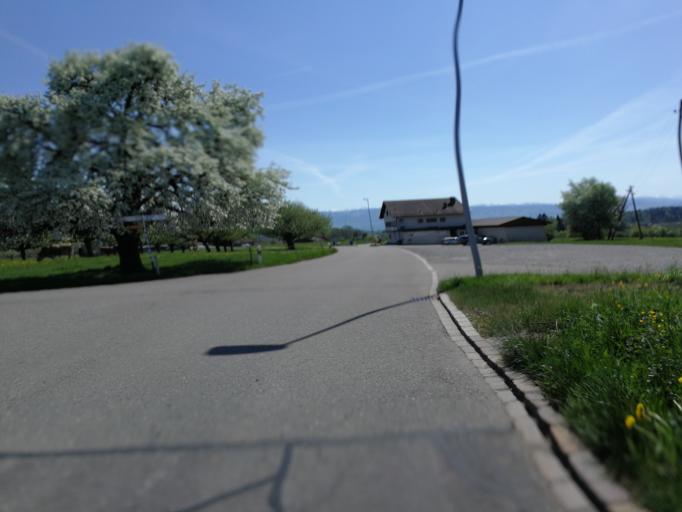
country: CH
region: Zurich
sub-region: Bezirk Hinwil
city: Durnten
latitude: 47.2857
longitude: 8.8238
